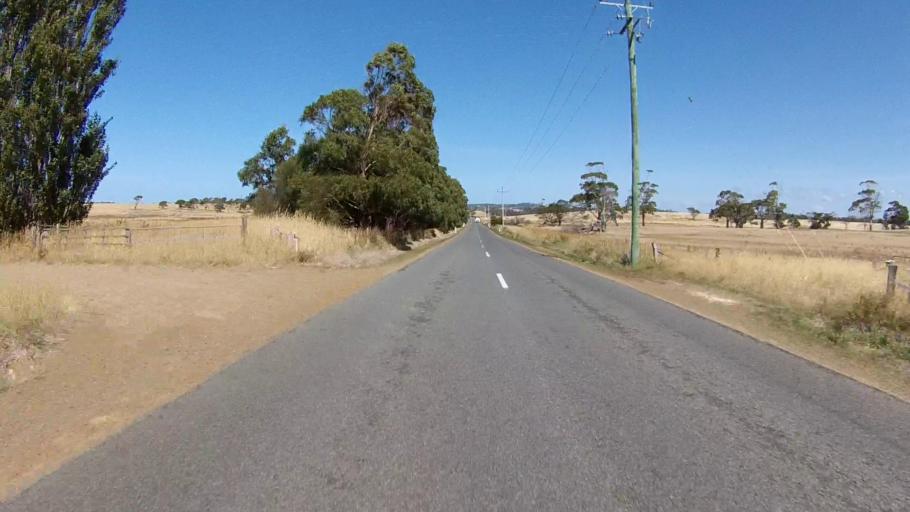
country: AU
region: Tasmania
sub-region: Sorell
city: Sorell
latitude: -42.2709
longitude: 148.0039
